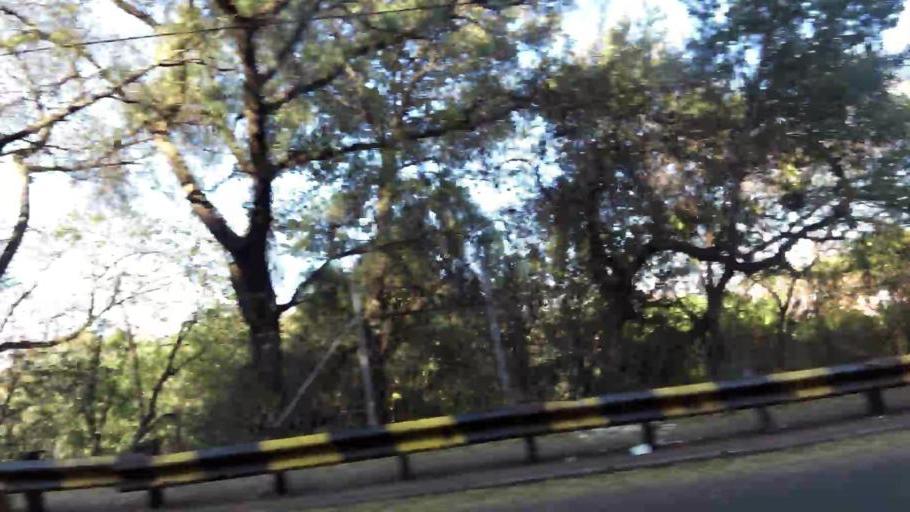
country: ZA
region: Gauteng
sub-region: City of Johannesburg Metropolitan Municipality
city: Johannesburg
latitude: -26.1720
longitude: 28.0137
